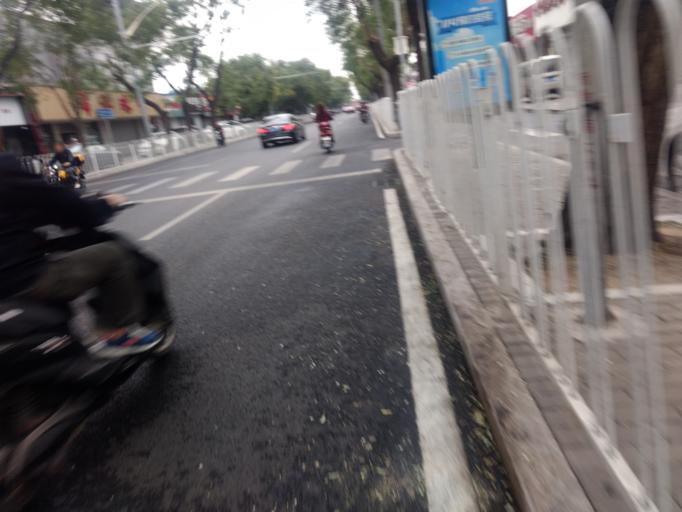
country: CN
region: Beijing
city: Jinrongjie
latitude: 39.9362
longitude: 116.3666
